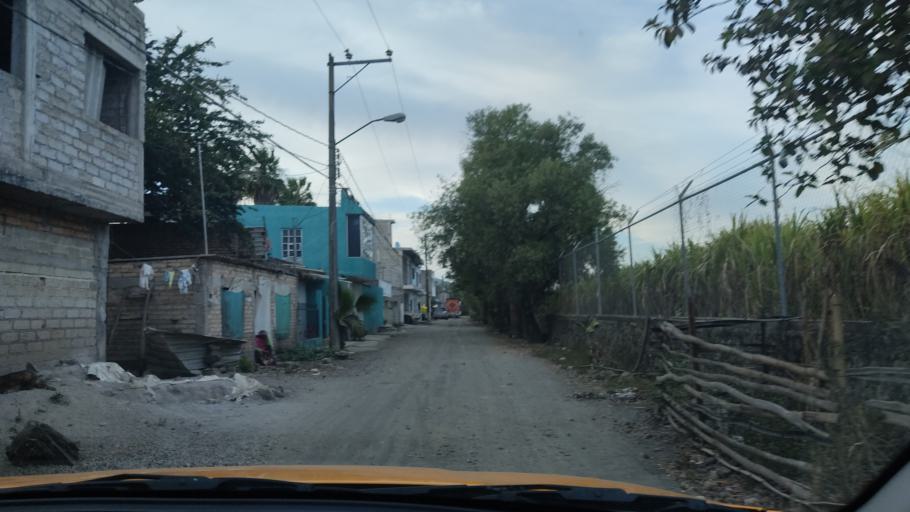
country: MX
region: Nayarit
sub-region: Tepic
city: La Corregidora
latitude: 21.4558
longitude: -104.8198
